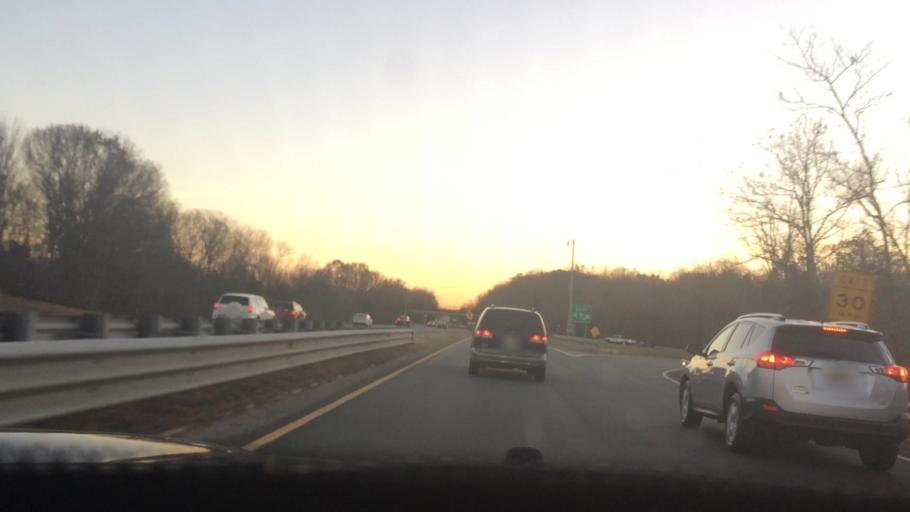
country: US
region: Massachusetts
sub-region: Essex County
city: Haverhill
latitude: 42.7772
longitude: -71.1184
